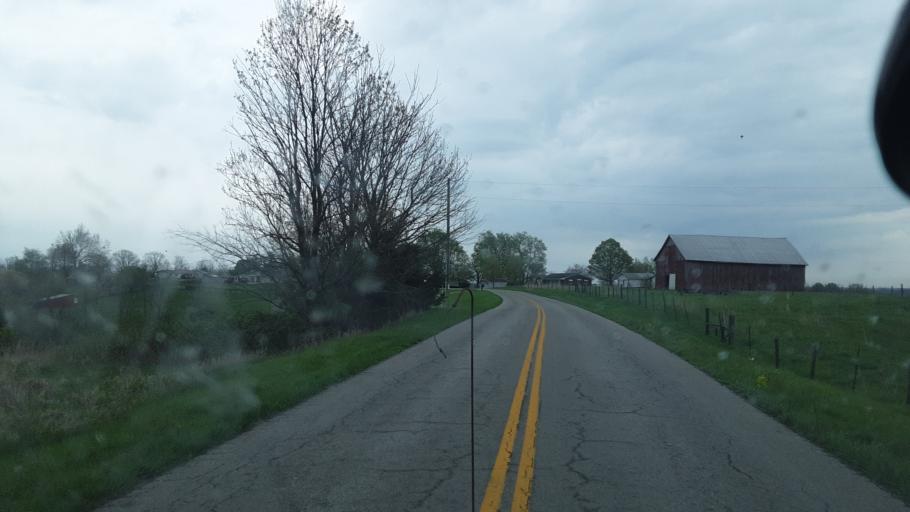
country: US
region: Kentucky
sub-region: Owen County
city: Owenton
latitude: 38.6243
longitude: -84.7850
